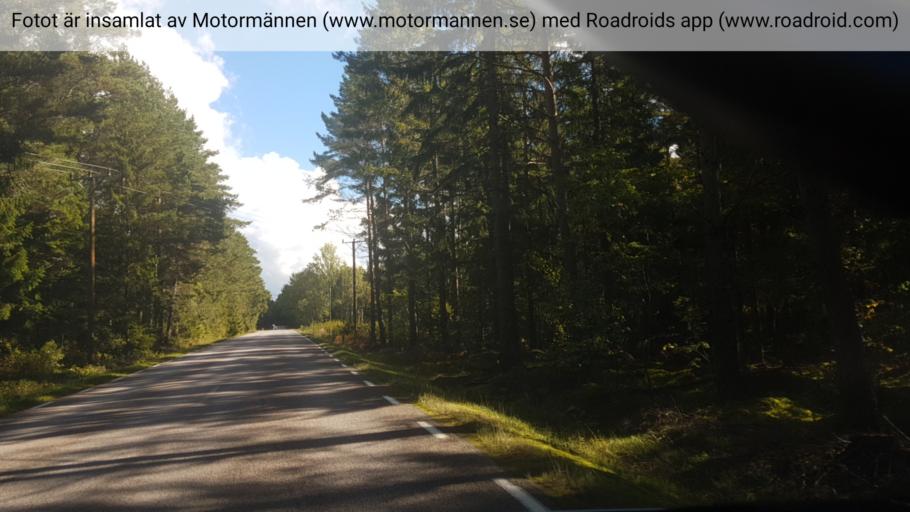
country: SE
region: Vaestra Goetaland
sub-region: Gotene Kommun
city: Goetene
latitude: 58.5459
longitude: 13.6428
